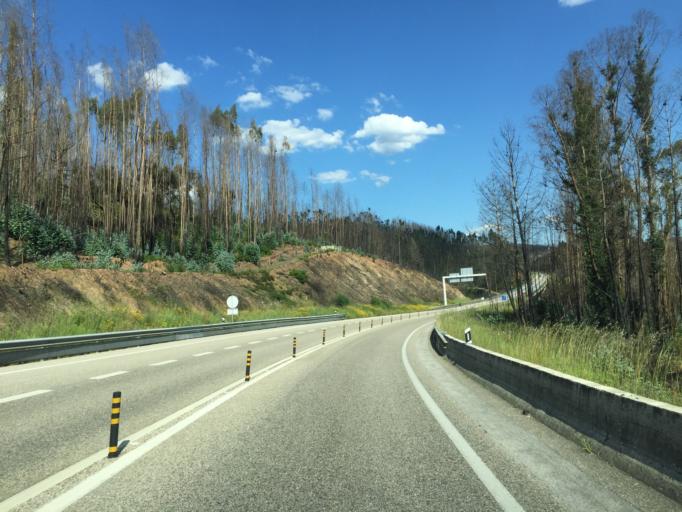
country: PT
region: Leiria
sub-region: Figueiro Dos Vinhos
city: Figueiro dos Vinhos
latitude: 39.9274
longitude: -8.3267
